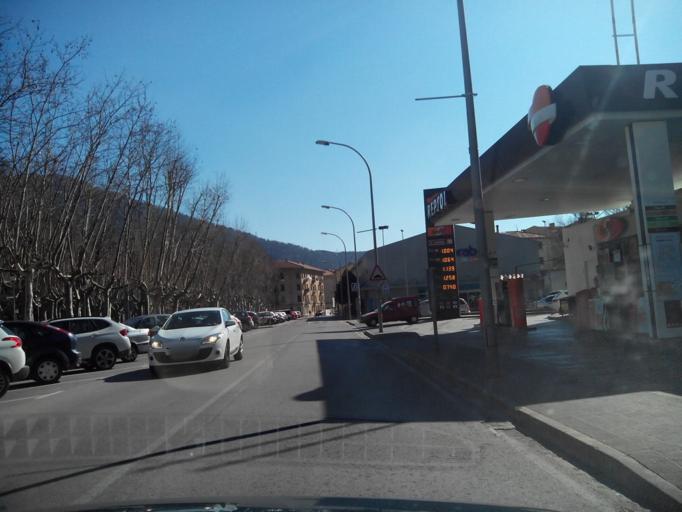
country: ES
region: Catalonia
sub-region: Provincia de Girona
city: Ripoll
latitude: 42.1976
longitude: 2.1906
